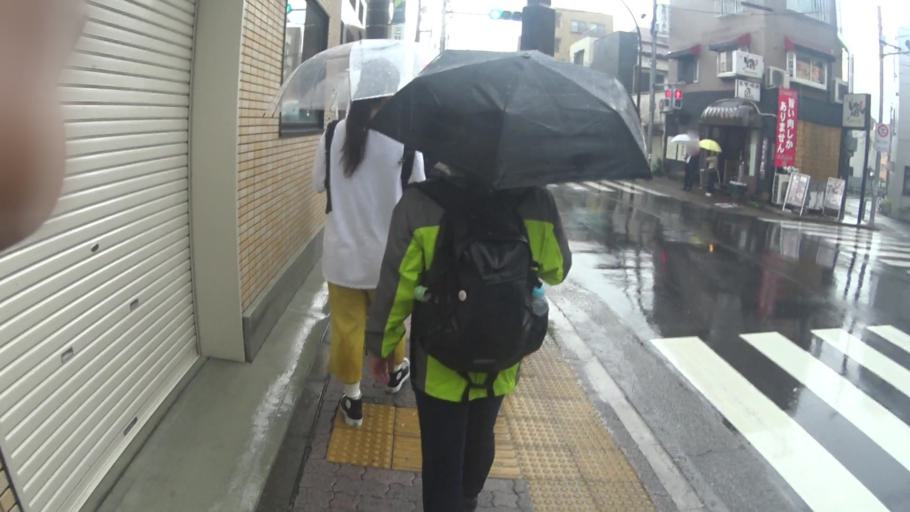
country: JP
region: Saitama
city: Wako
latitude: 35.7507
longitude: 139.6650
